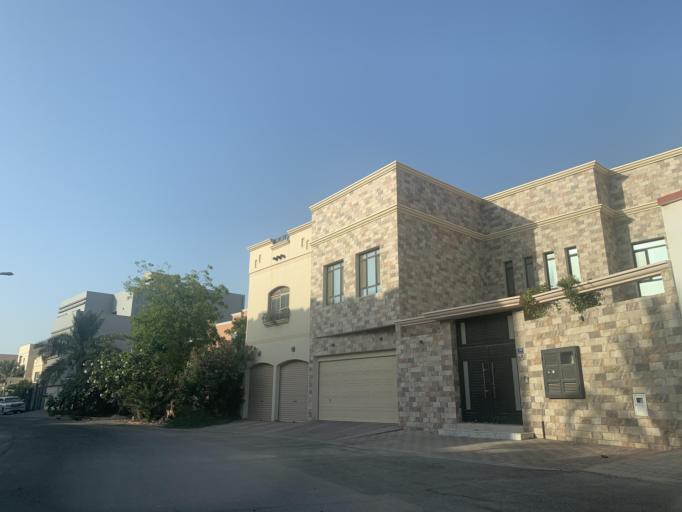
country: BH
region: Manama
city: Jidd Hafs
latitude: 26.2106
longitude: 50.5273
